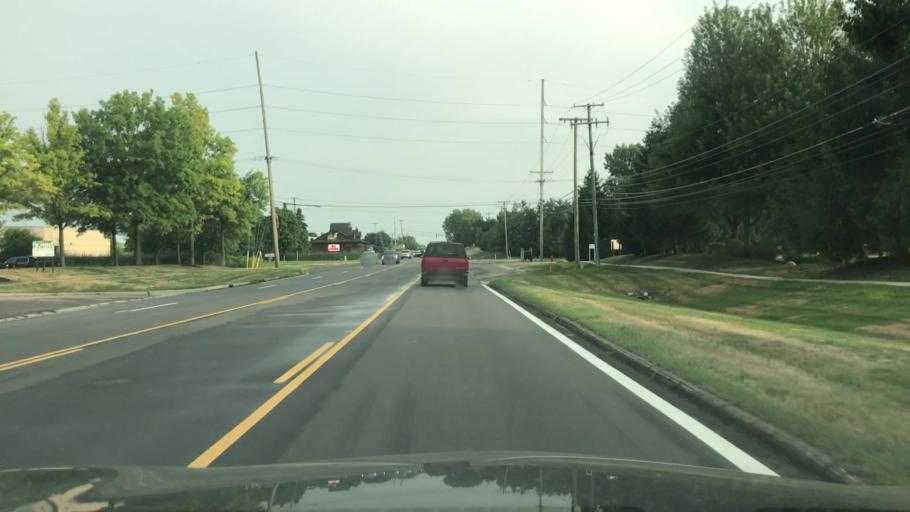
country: US
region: Michigan
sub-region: Oakland County
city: Novi
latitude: 42.4927
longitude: -83.4361
